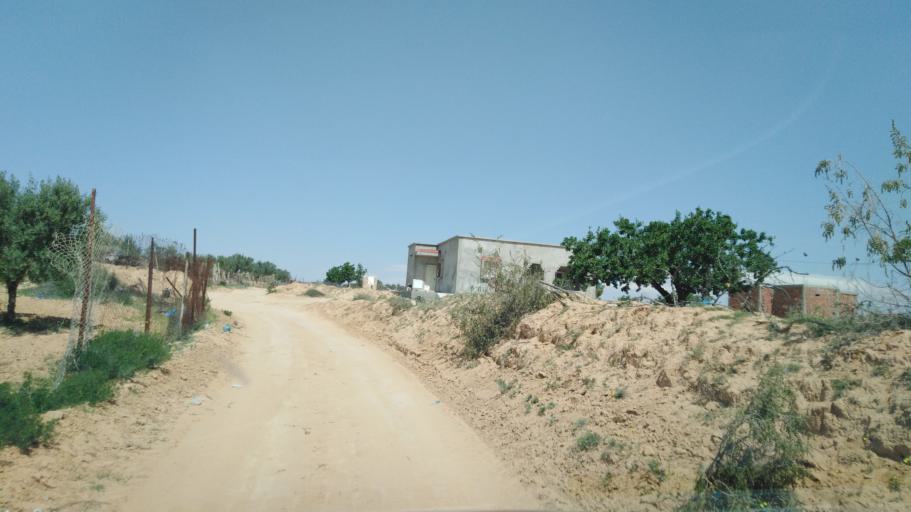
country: TN
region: Safaqis
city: Sfax
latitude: 34.7643
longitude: 10.5195
